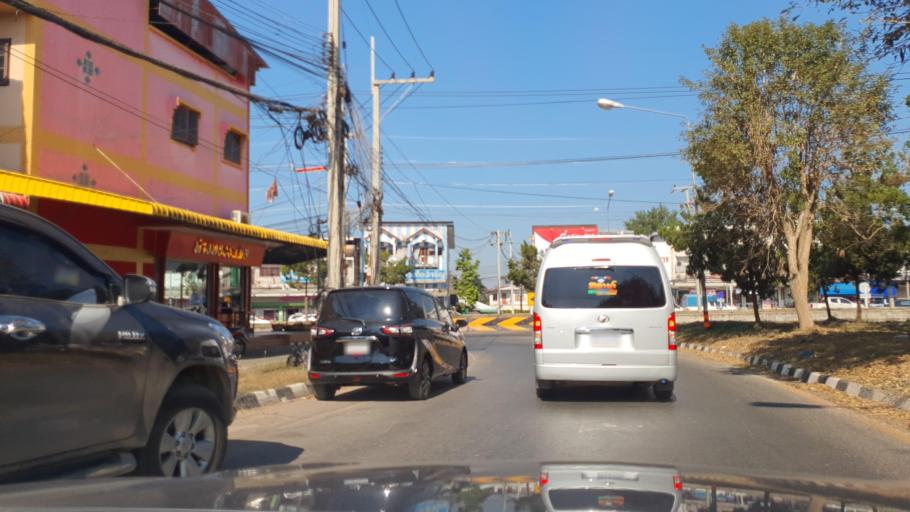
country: TH
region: Nan
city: Pua
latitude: 19.1773
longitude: 100.9155
